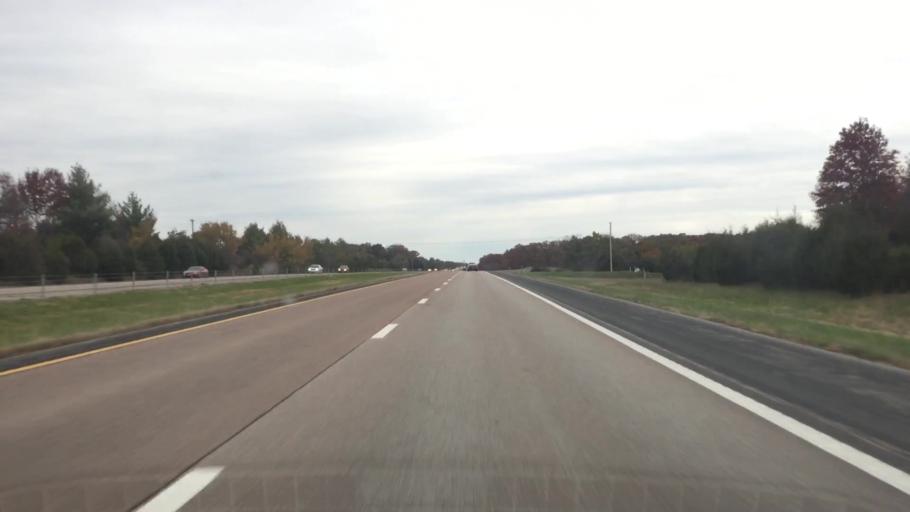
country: US
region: Missouri
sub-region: Boone County
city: Ashland
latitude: 38.7181
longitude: -92.2542
